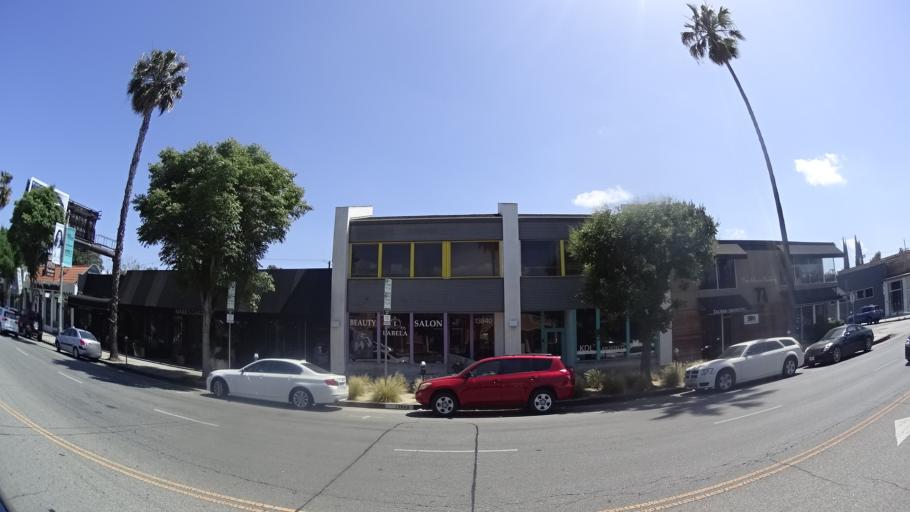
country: US
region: California
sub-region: Los Angeles County
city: Sherman Oaks
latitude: 34.1486
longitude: -118.4345
